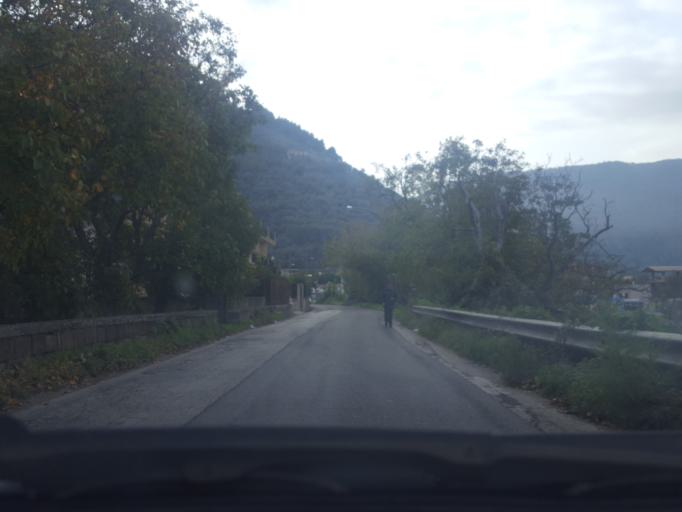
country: IT
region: Campania
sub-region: Provincia di Caserta
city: Arienzo
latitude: 41.0246
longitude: 14.4918
